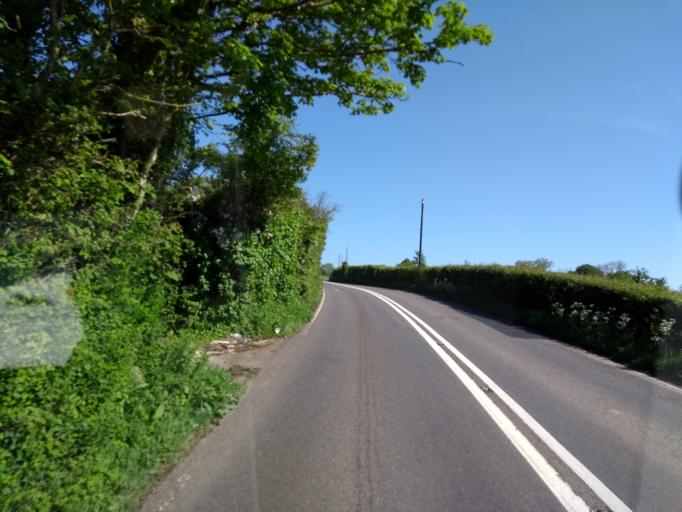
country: GB
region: England
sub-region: Devon
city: Axminster
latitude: 50.8207
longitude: -2.9700
